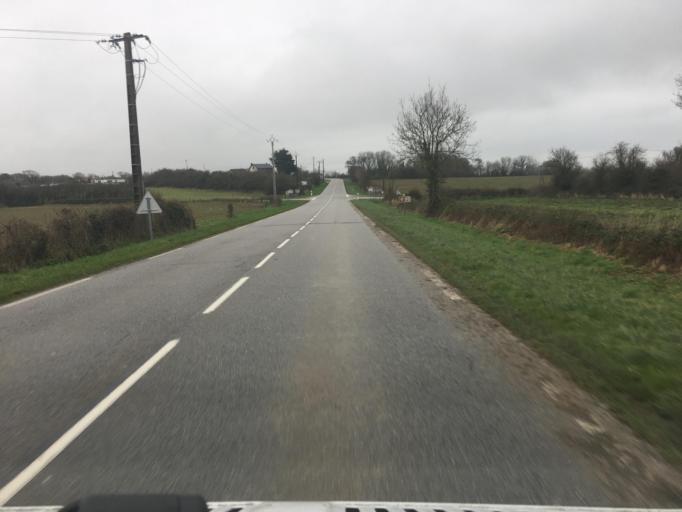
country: FR
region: Lower Normandy
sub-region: Departement de la Manche
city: Montebourg
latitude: 49.5203
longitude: -1.3182
